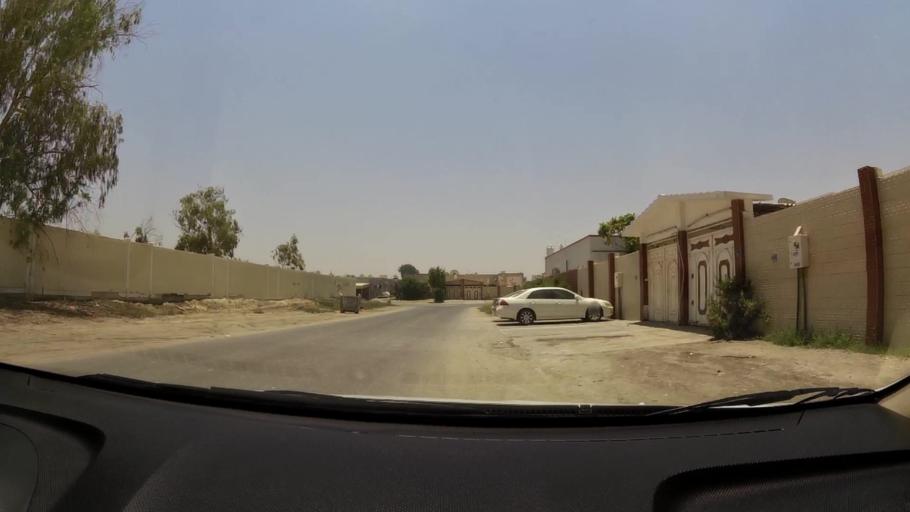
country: AE
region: Umm al Qaywayn
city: Umm al Qaywayn
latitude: 25.5491
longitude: 55.5480
